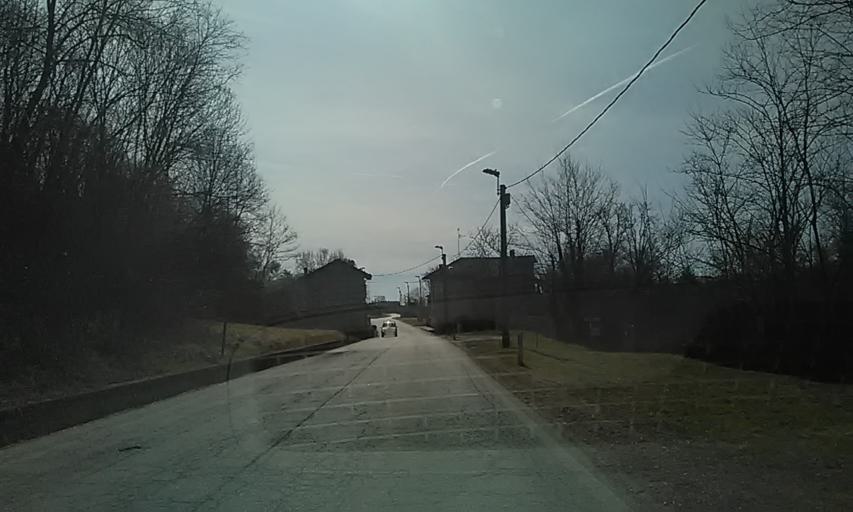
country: IT
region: Piedmont
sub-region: Provincia di Biella
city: Brusnengo
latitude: 45.6022
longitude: 8.2437
